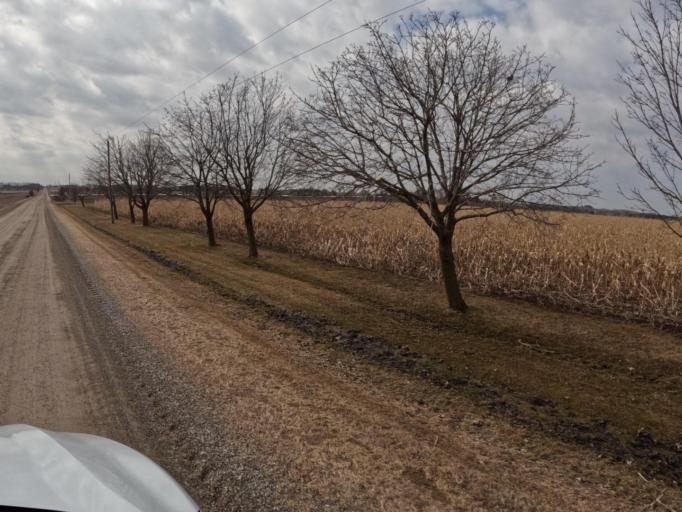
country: CA
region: Ontario
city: Orangeville
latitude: 43.9354
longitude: -80.2427
